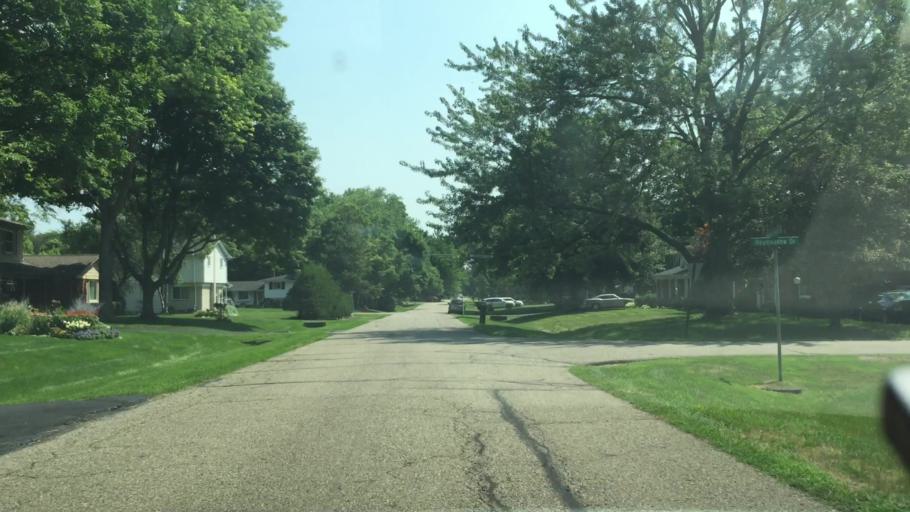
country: US
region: Michigan
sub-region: Oakland County
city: West Bloomfield Township
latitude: 42.5374
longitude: -83.3550
